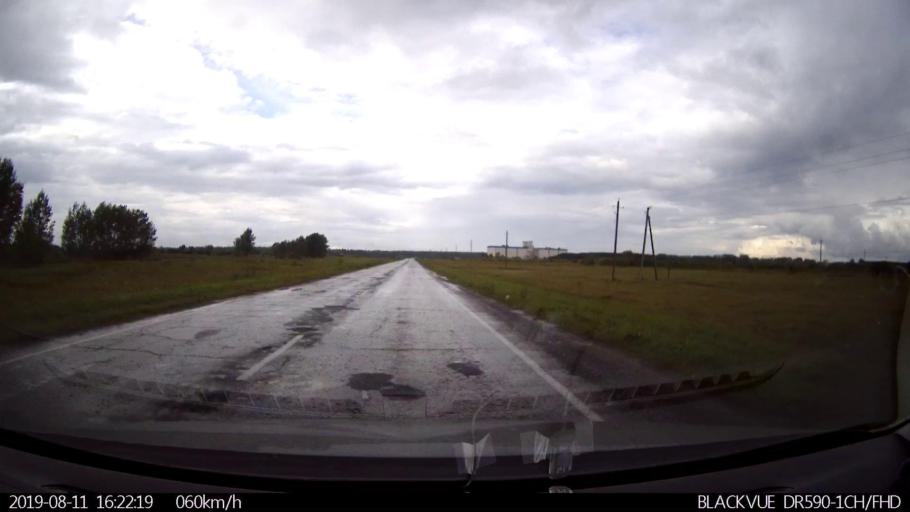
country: RU
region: Ulyanovsk
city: Mayna
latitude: 54.0870
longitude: 47.5935
